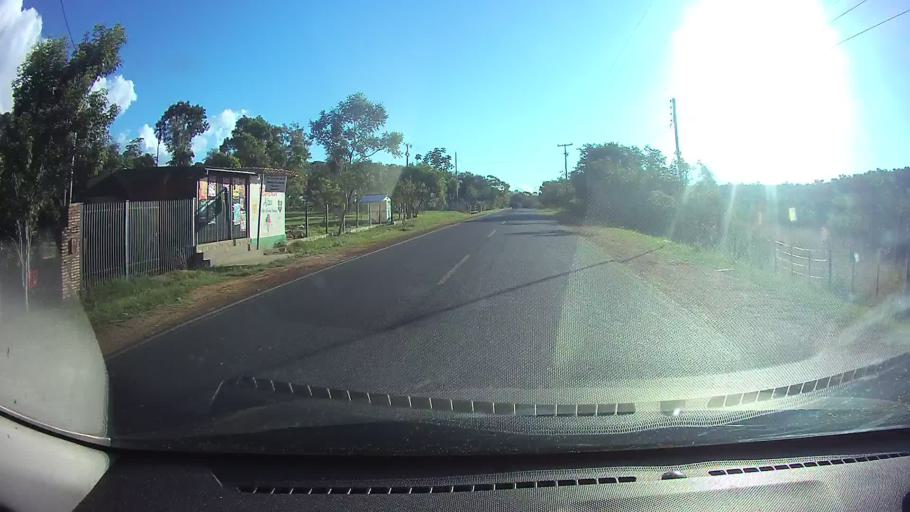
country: PY
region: Cordillera
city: Emboscada
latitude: -25.1688
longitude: -57.2749
